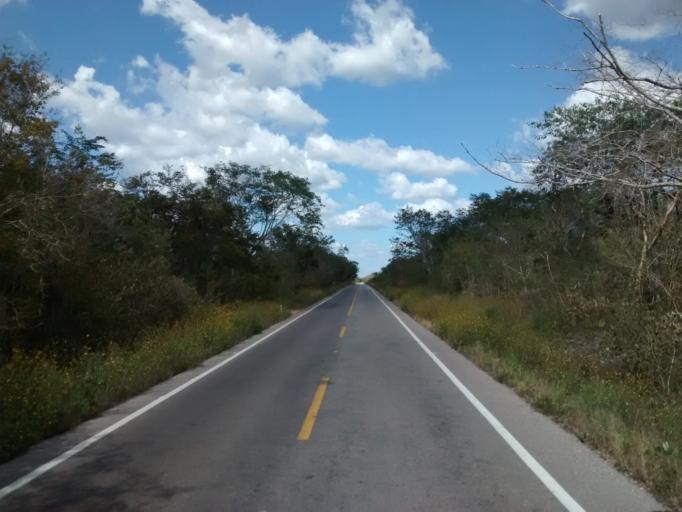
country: MX
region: Yucatan
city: Chichimila
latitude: 20.5146
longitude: -88.2704
